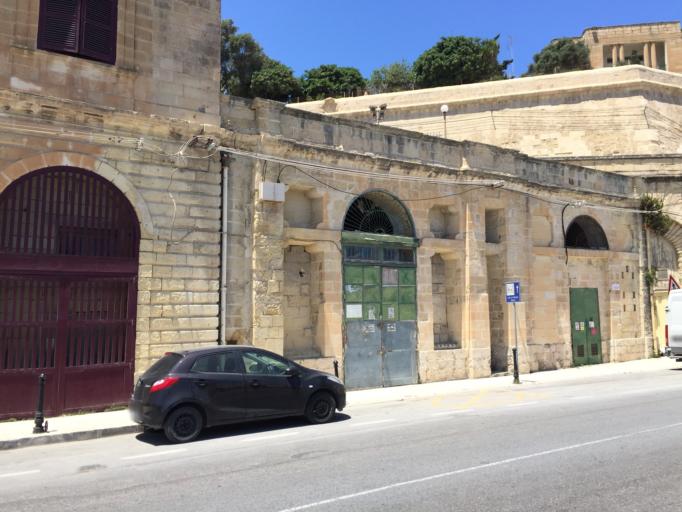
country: MT
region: Il-Furjana
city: Floriana
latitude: 35.8922
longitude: 14.5099
